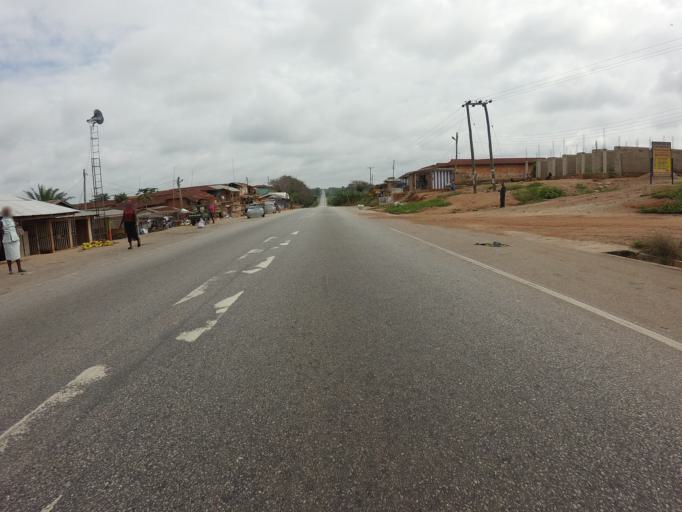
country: GH
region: Ashanti
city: Mampong
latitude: 7.0520
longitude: -1.7105
